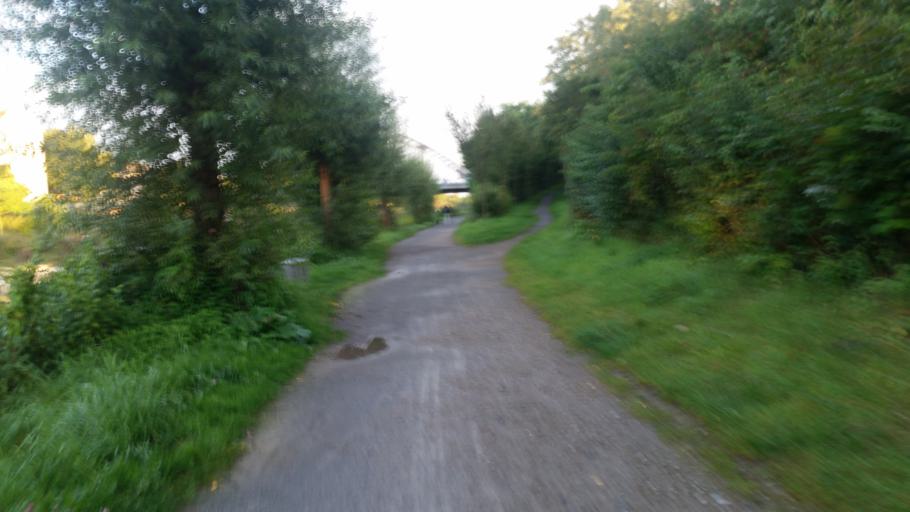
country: DE
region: Lower Saxony
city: Isernhagen Farster Bauerschaft
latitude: 52.4011
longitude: 9.8193
